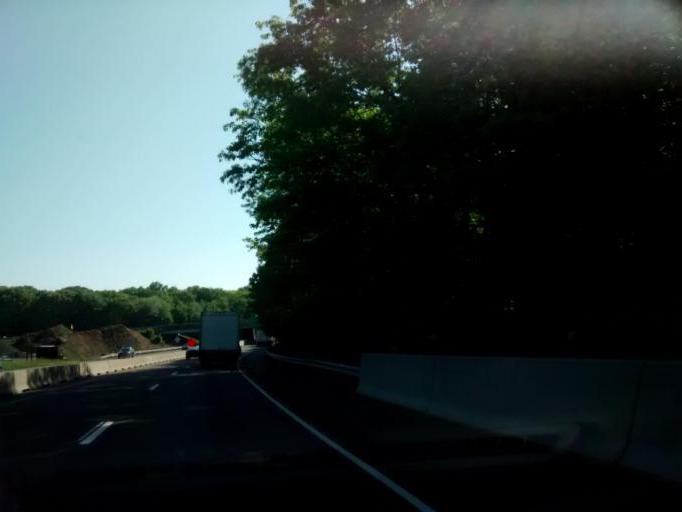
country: US
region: Connecticut
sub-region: New London County
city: Niantic
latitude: 41.3266
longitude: -72.2482
